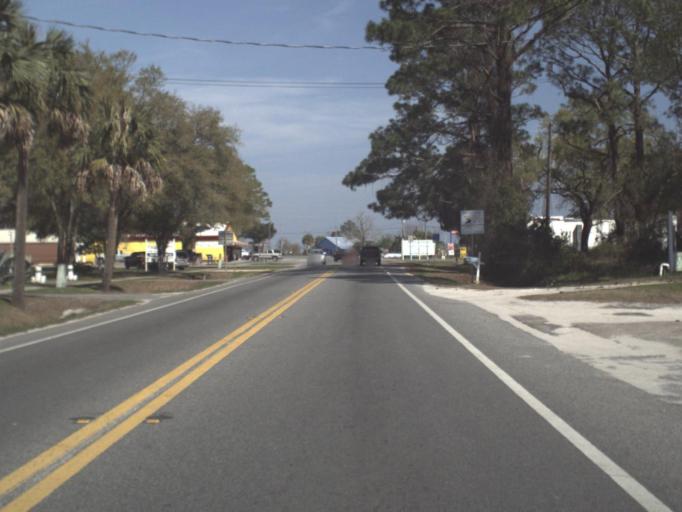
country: US
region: Florida
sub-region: Franklin County
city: Eastpoint
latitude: 29.7365
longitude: -84.8809
